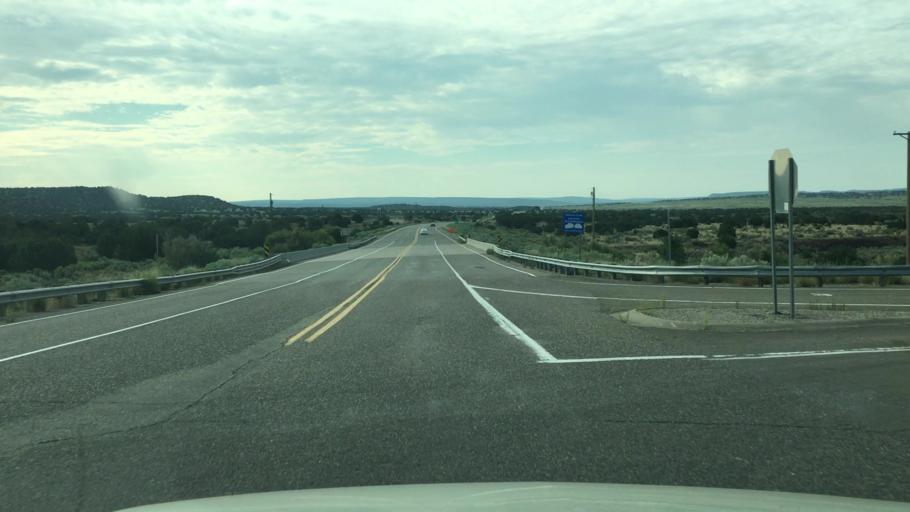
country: US
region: New Mexico
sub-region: Santa Fe County
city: Eldorado at Santa Fe
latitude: 35.4634
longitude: -105.8985
